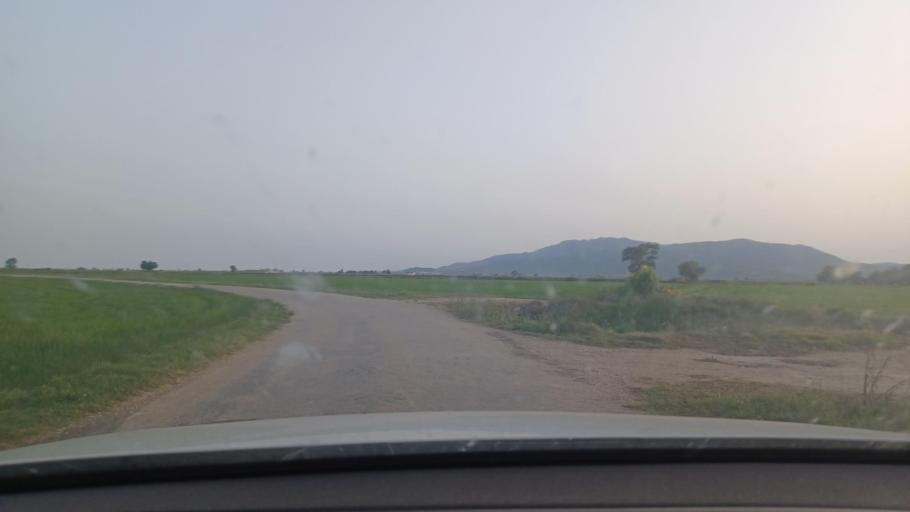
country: ES
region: Catalonia
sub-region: Provincia de Tarragona
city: Deltebre
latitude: 40.6918
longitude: 0.6517
